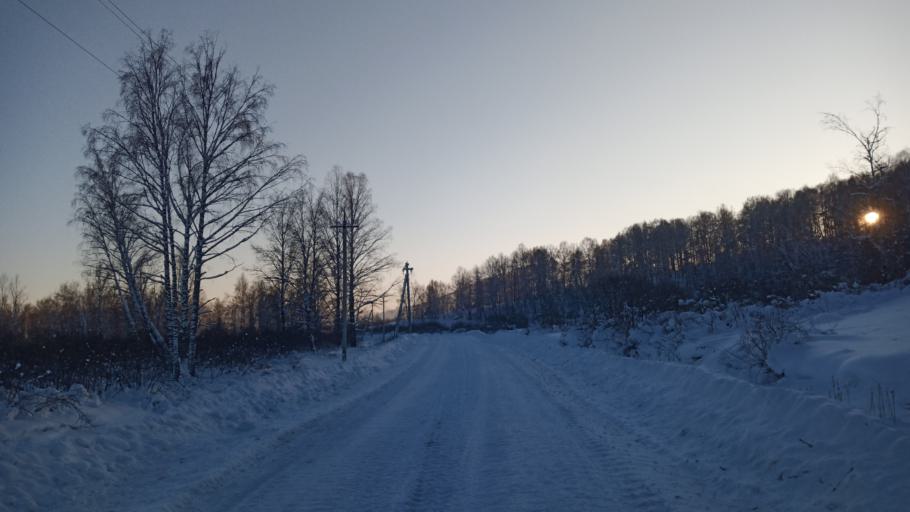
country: RU
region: Altai Krai
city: Krasnogorskoye
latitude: 52.1262
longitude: 86.2046
